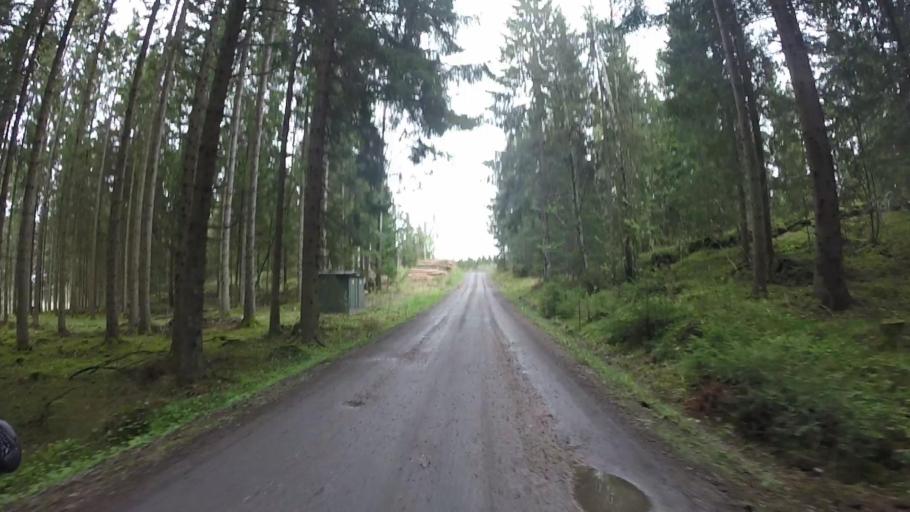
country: SE
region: Vaestra Goetaland
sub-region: Trollhattan
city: Sjuntorp
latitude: 58.2207
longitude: 12.2201
